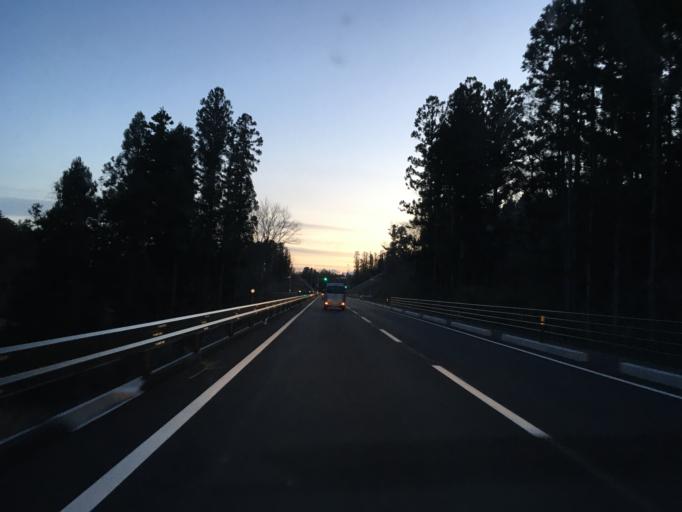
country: JP
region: Miyagi
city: Wakuya
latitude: 38.7252
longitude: 141.2794
